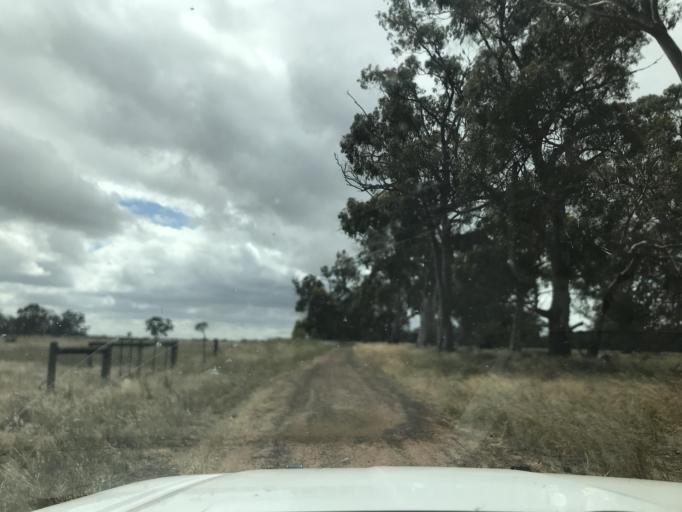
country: AU
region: South Australia
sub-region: Naracoorte and Lucindale
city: Naracoorte
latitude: -36.9015
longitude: 141.4125
